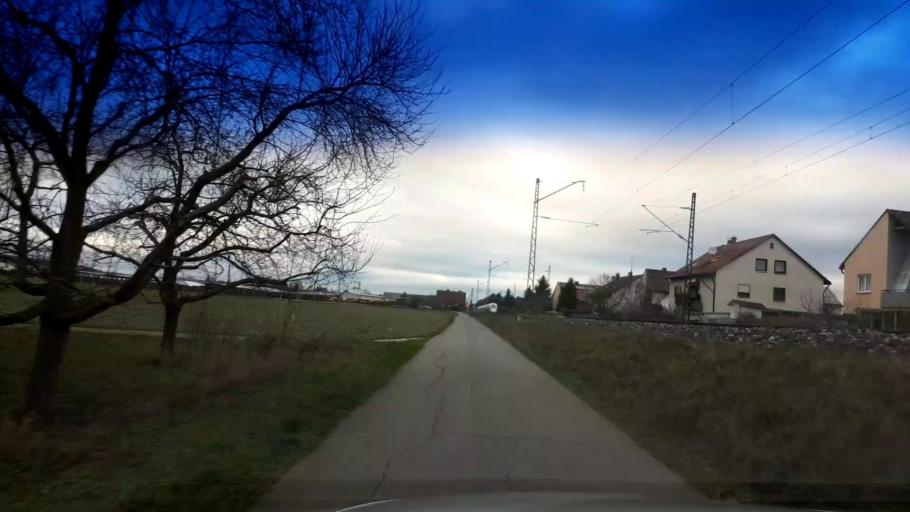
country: DE
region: Bavaria
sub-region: Upper Franconia
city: Strullendorf
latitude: 49.8401
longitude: 10.9676
